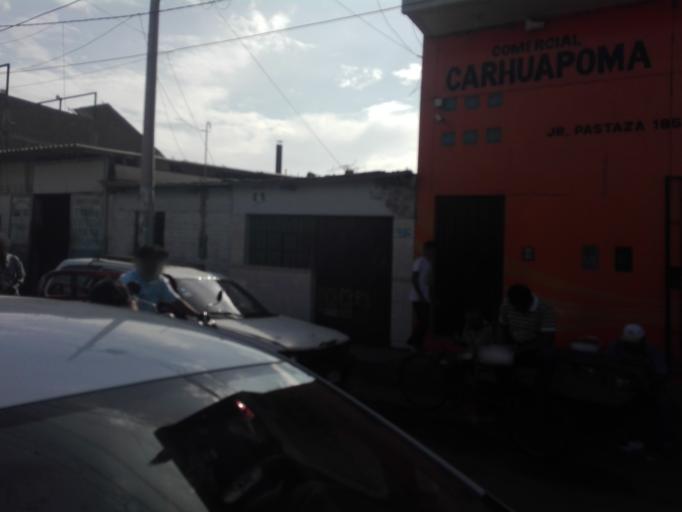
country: PE
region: Piura
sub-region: Provincia de Piura
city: Piura
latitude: -5.1867
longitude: -80.6330
